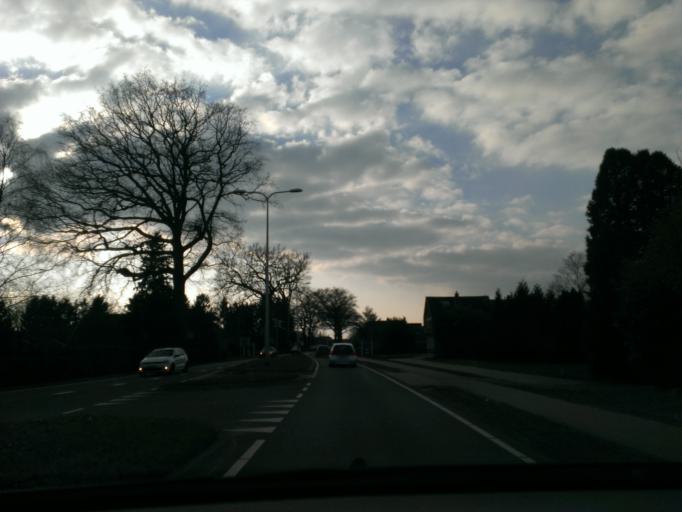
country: NL
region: Overijssel
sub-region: Gemeente Twenterand
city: Den Ham
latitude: 52.3636
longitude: 6.4895
